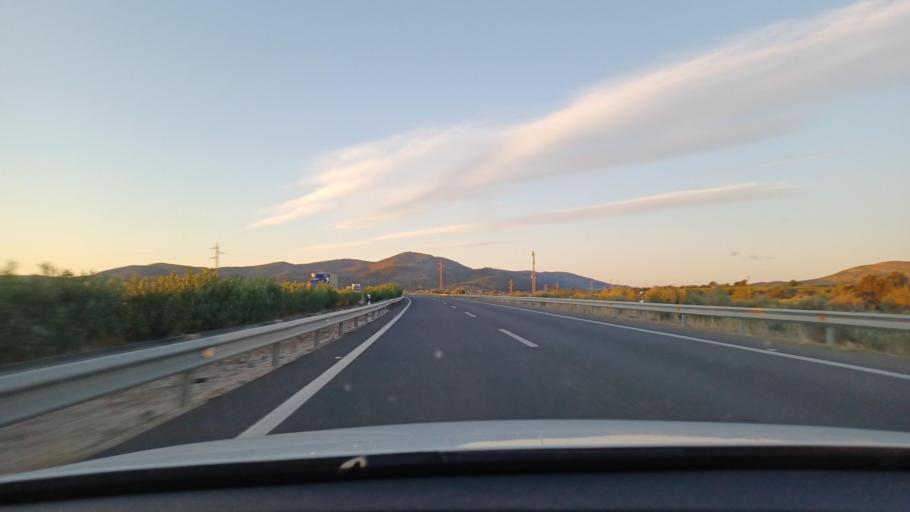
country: ES
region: Valencia
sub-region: Provincia de Castello
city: Calig
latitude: 40.4137
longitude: 0.3728
